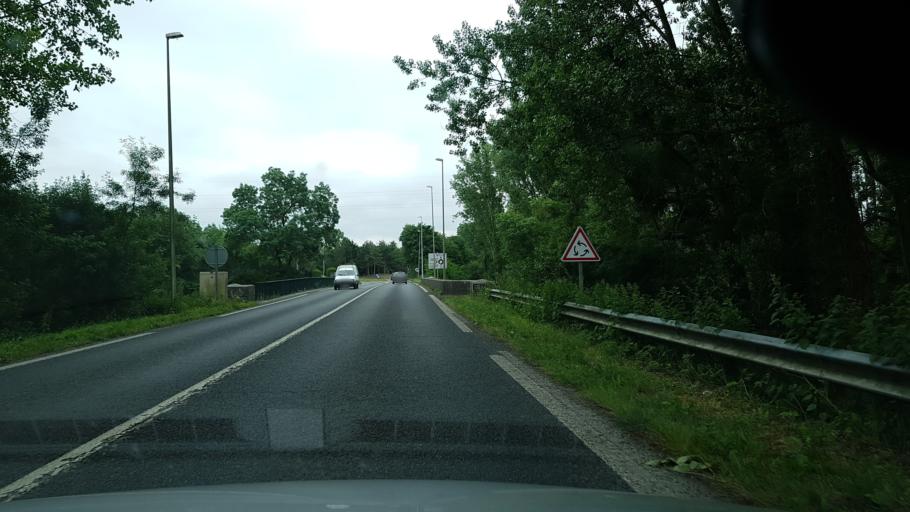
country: FR
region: Centre
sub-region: Departement du Loir-et-Cher
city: Selles-sur-Cher
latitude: 47.2876
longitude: 1.5345
